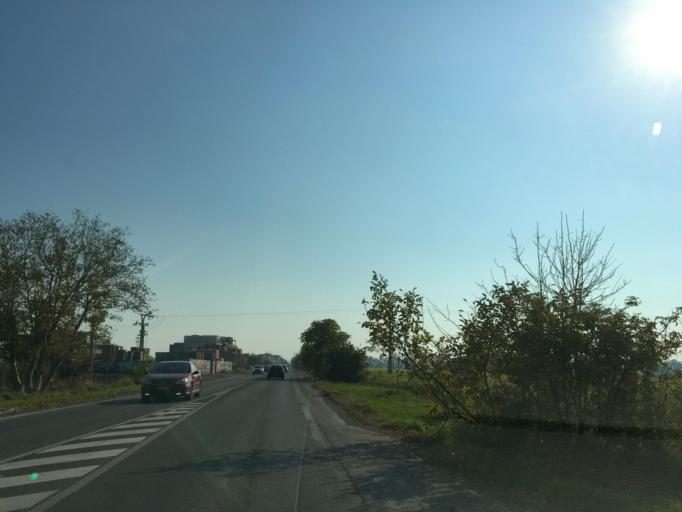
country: SK
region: Bratislavsky
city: Dunajska Luzna
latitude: 48.0753
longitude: 17.2714
